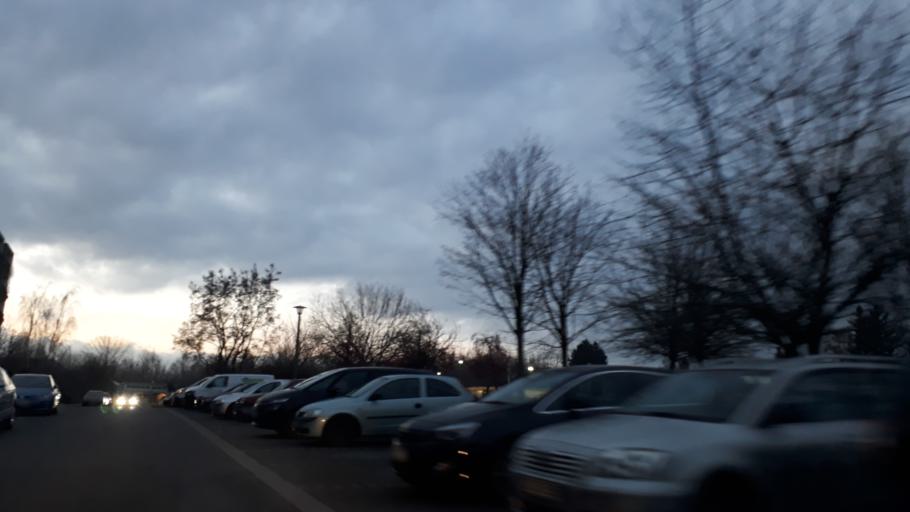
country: DE
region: Saxony
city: Freital
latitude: 51.0470
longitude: 13.6642
